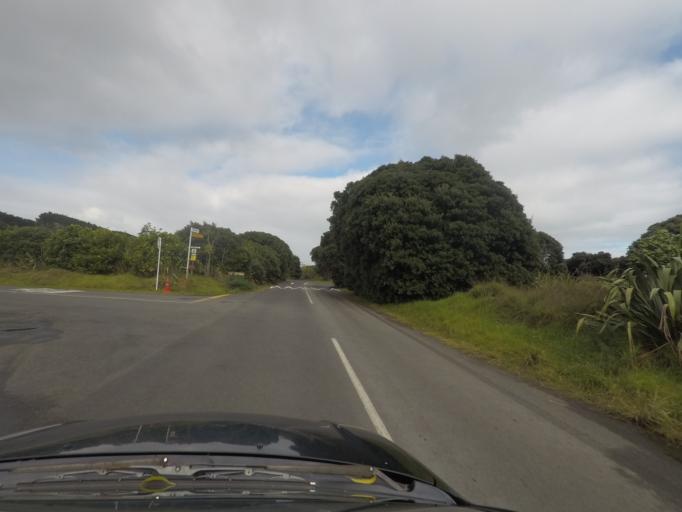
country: NZ
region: Auckland
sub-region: Auckland
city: Muriwai Beach
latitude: -36.8893
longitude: 174.4503
